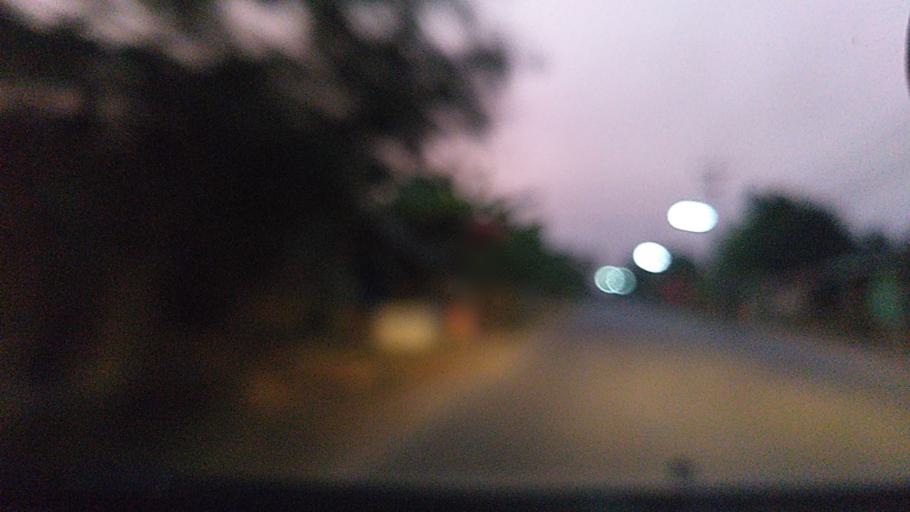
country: TH
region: Sing Buri
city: Sing Buri
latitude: 14.8374
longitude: 100.3956
